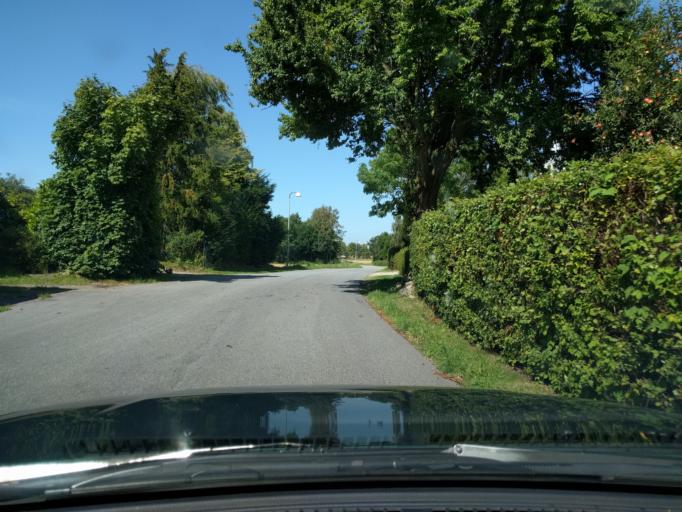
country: DK
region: Zealand
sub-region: Vordingborg Kommune
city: Orslev
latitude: 55.0783
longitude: 11.9477
